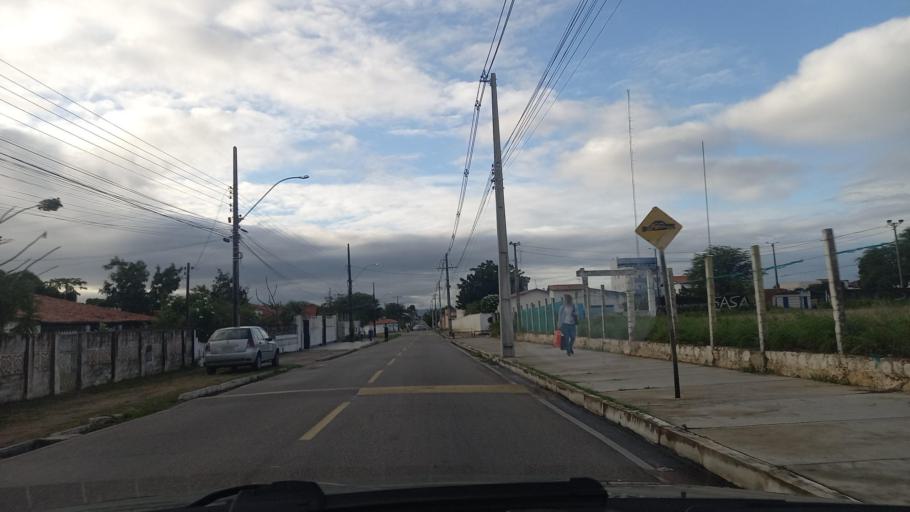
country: BR
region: Bahia
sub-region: Paulo Afonso
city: Paulo Afonso
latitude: -9.3963
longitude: -38.2317
